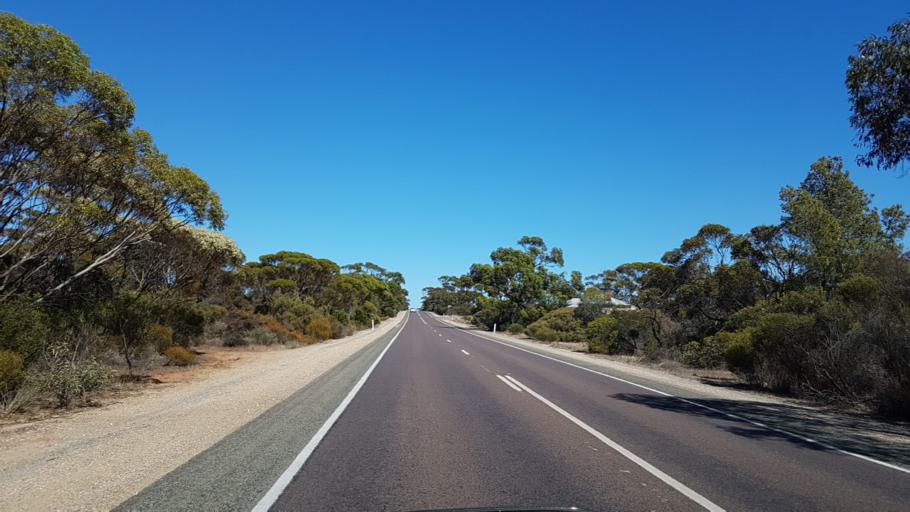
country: AU
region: South Australia
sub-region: Copper Coast
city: Kadina
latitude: -34.0486
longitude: 137.9672
